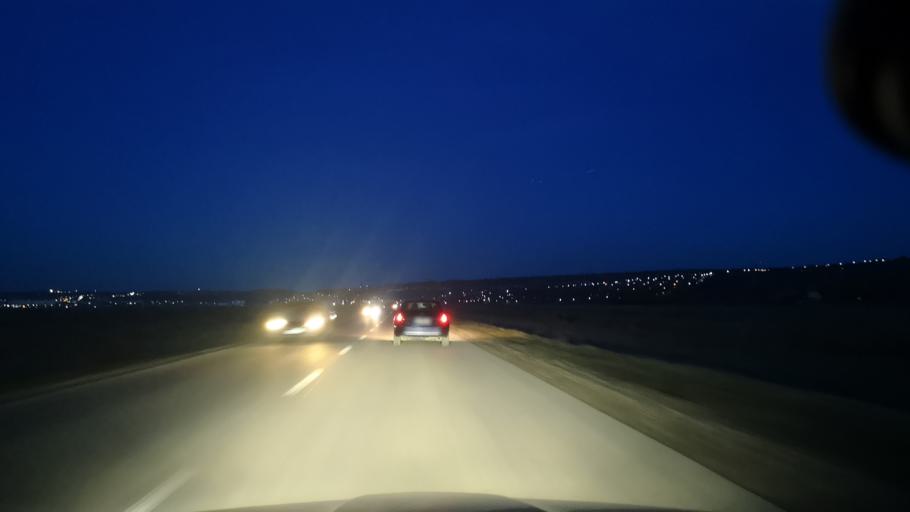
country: MD
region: Orhei
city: Orhei
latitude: 47.3451
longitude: 28.7844
